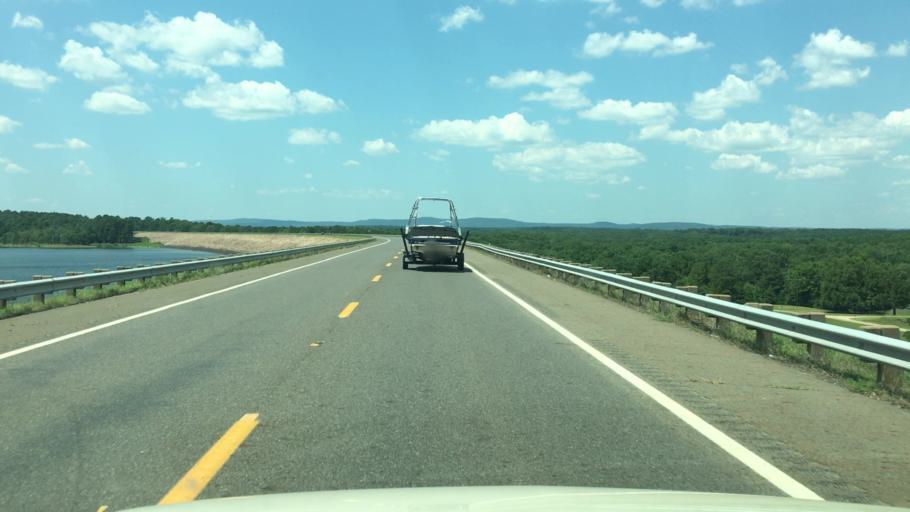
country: US
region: Arkansas
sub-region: Clark County
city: Arkadelphia
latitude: 34.2376
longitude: -93.1029
